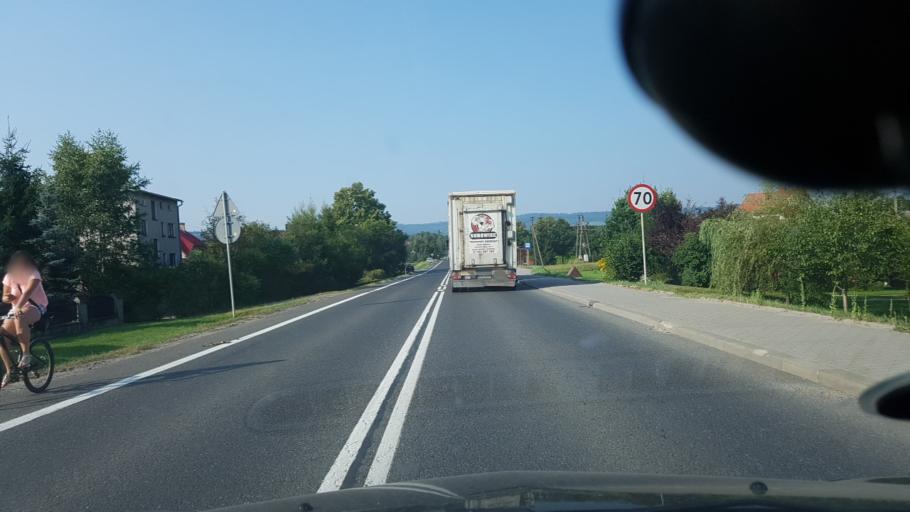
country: PL
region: Lesser Poland Voivodeship
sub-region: Powiat nowotarski
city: Rokiciny
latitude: 49.5980
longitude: 19.9199
